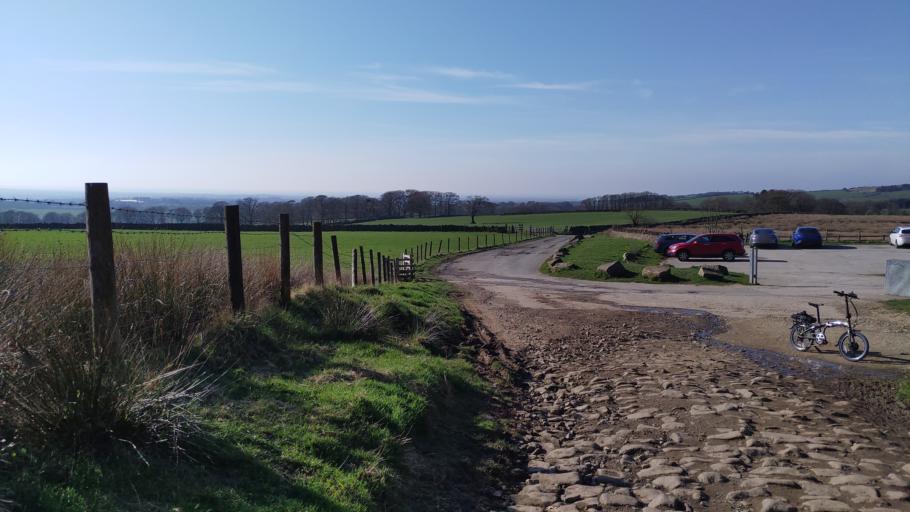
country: GB
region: England
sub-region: Borough of Bolton
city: Horwich
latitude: 53.6286
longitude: -2.5488
